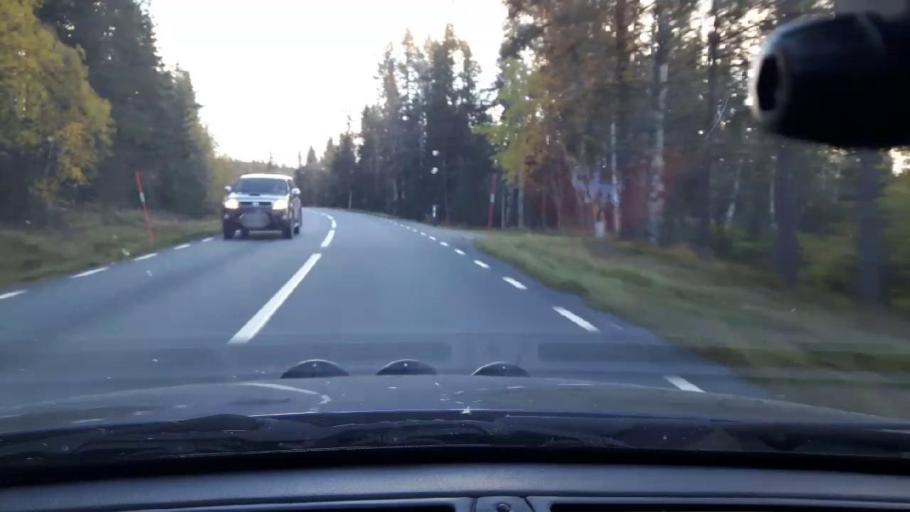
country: SE
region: Jaemtland
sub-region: Bergs Kommun
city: Hoverberg
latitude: 63.0520
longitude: 14.3271
